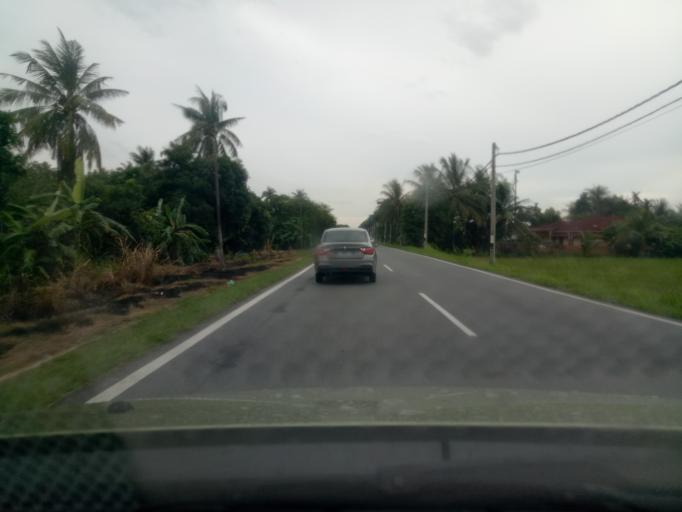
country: MY
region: Kedah
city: Gurun
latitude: 5.9700
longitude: 100.4224
